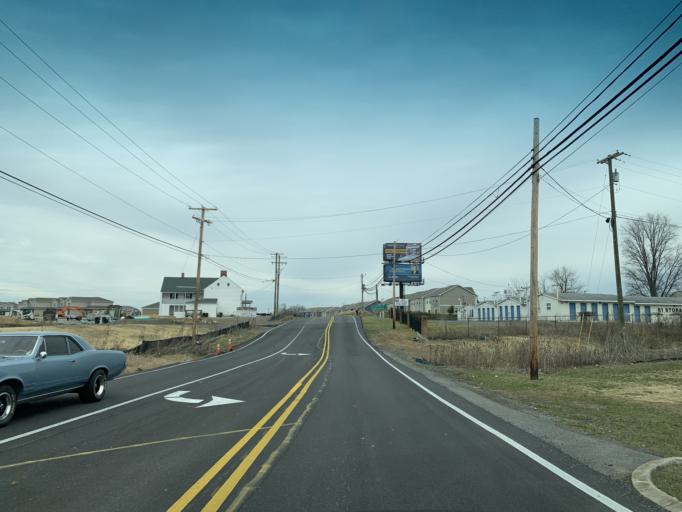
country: US
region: Maryland
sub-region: Washington County
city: Williamsport
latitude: 39.5450
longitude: -77.9050
